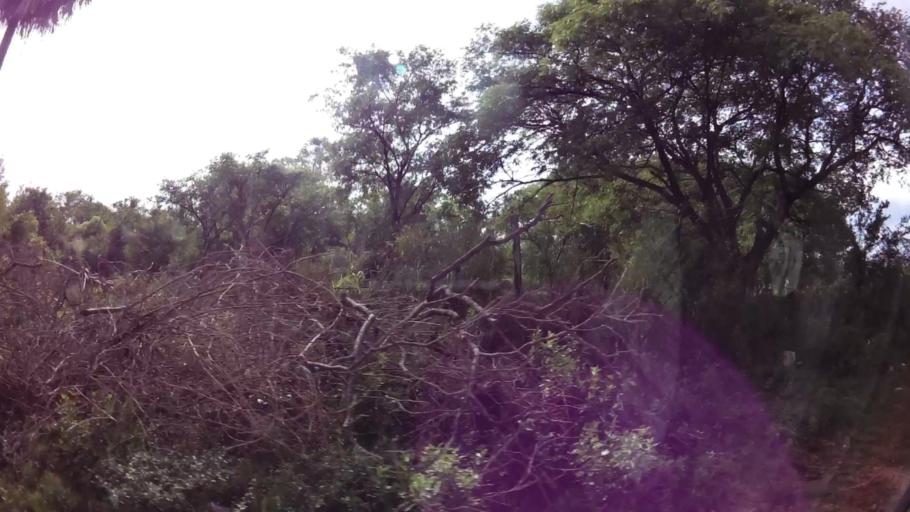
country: PY
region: Central
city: Limpio
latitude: -25.1730
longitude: -57.4942
